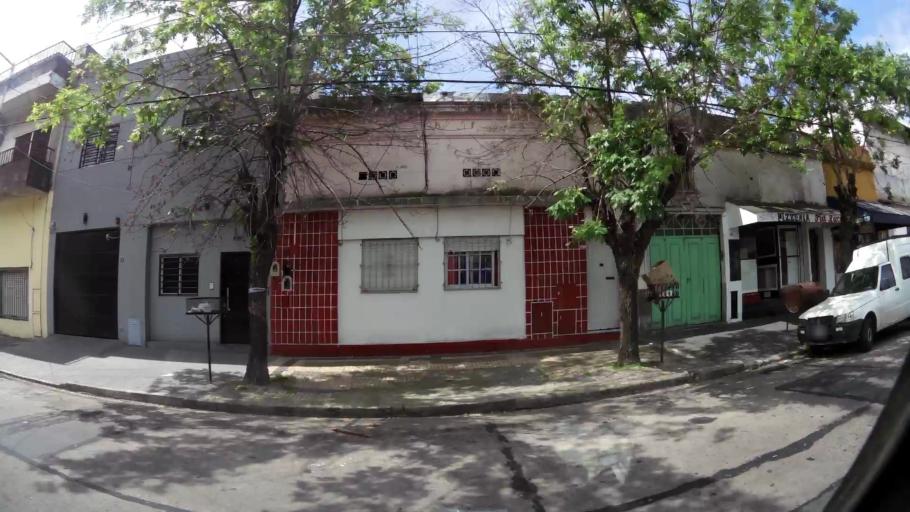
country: AR
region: Buenos Aires
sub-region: Partido de Avellaneda
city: Avellaneda
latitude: -34.6691
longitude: -58.3952
